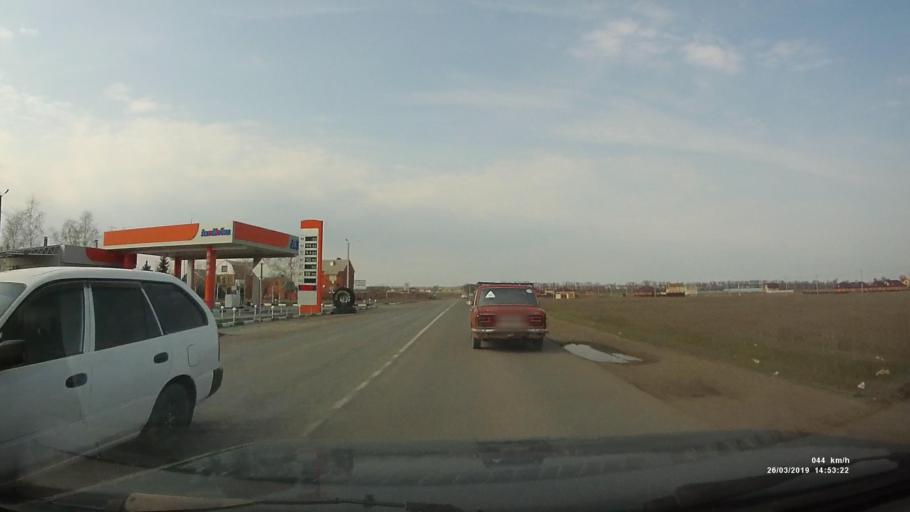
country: RU
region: Rostov
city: Novobessergenovka
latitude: 47.1842
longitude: 38.8145
